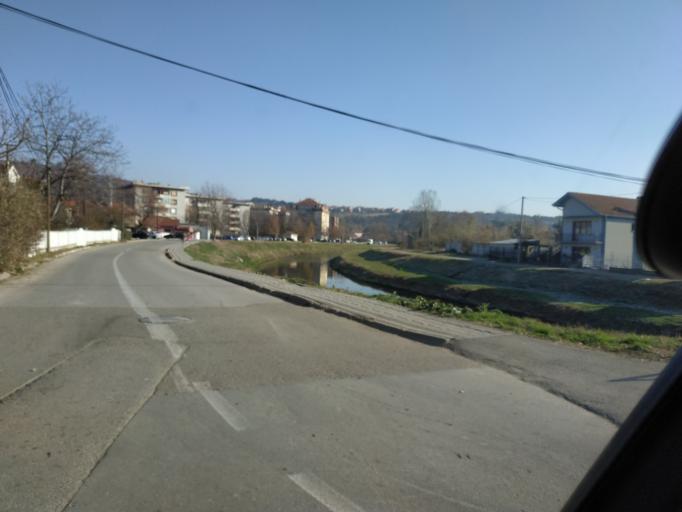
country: RS
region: Central Serbia
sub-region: Nisavski Okrug
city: Aleksinac
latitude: 43.5372
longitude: 21.7035
